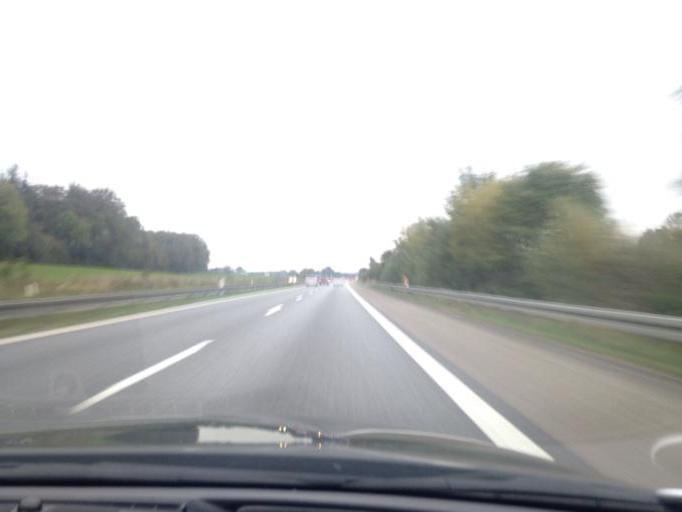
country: DK
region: South Denmark
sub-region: Haderslev Kommune
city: Haderslev
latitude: 55.3026
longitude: 9.4309
